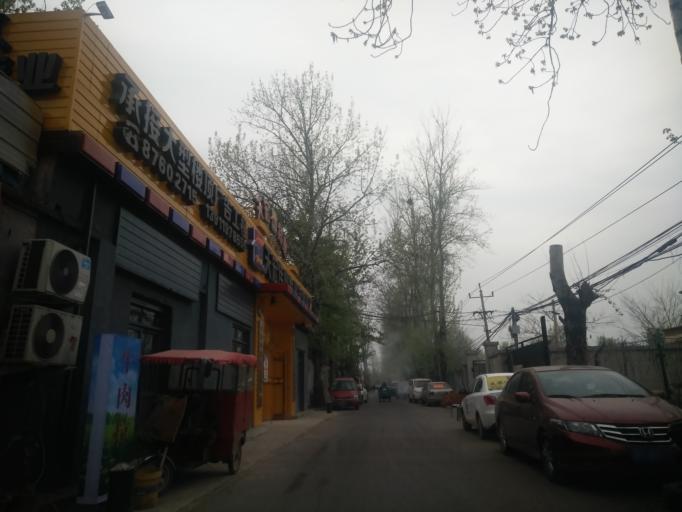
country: CN
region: Beijing
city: Jiugong
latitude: 39.8150
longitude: 116.4748
